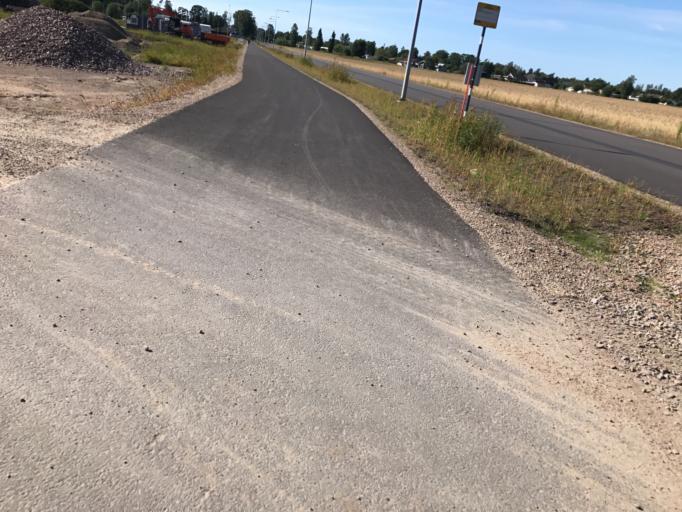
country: SE
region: Skane
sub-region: Bastads Kommun
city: Bastad
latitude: 56.4338
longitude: 12.9074
